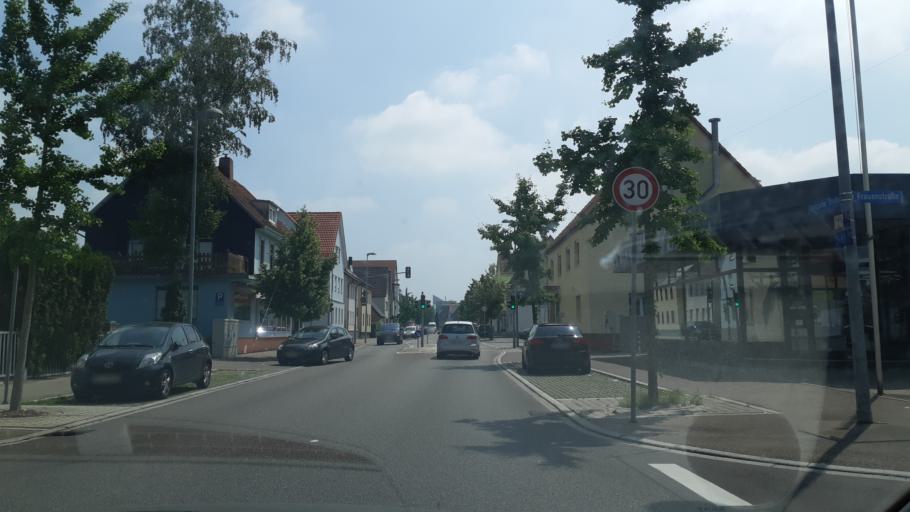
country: DE
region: Baden-Wuerttemberg
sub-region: Regierungsbezirk Stuttgart
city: Eislingen
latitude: 48.6950
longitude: 9.6999
